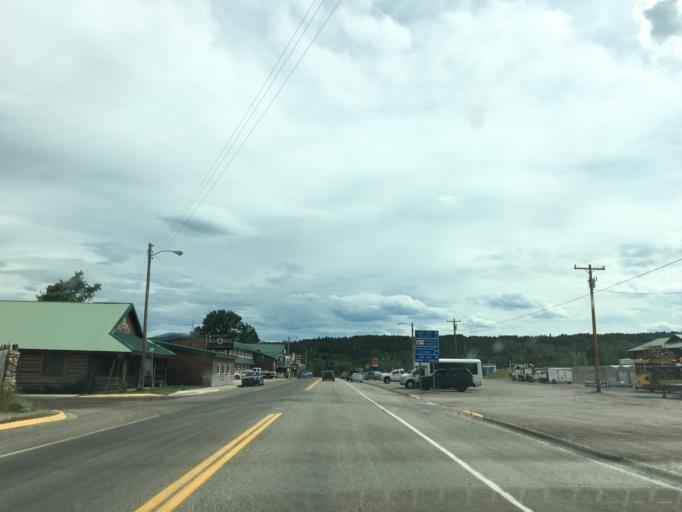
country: US
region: Montana
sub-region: Glacier County
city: South Browning
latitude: 48.4433
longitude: -113.2181
